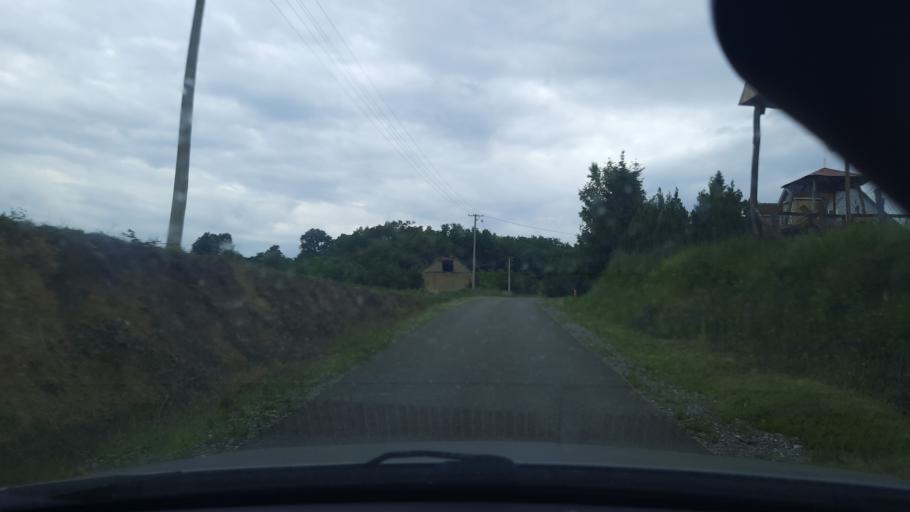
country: RS
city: Jarebice
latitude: 44.4919
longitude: 19.4791
